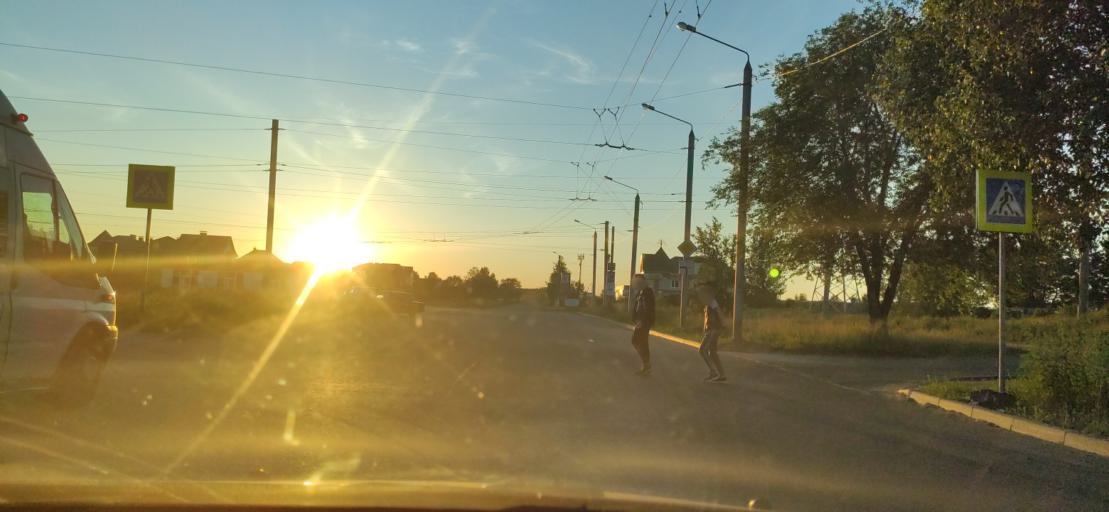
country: RU
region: Ulyanovsk
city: Mirnyy
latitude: 54.3882
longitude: 48.6128
